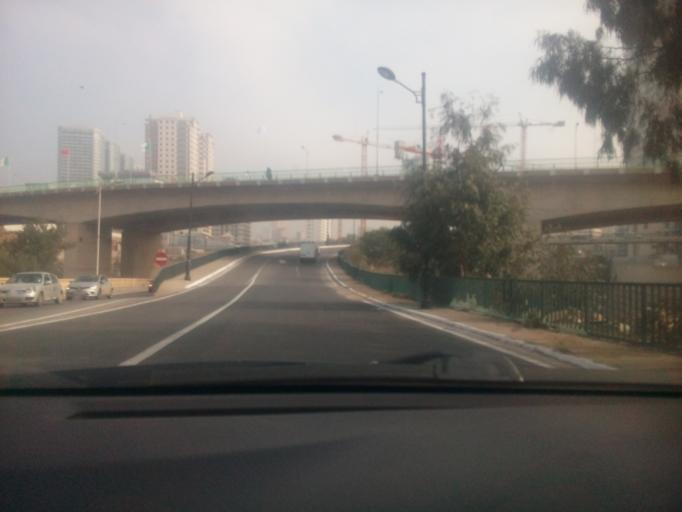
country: DZ
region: Oran
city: Oran
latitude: 35.7075
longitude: -0.6301
